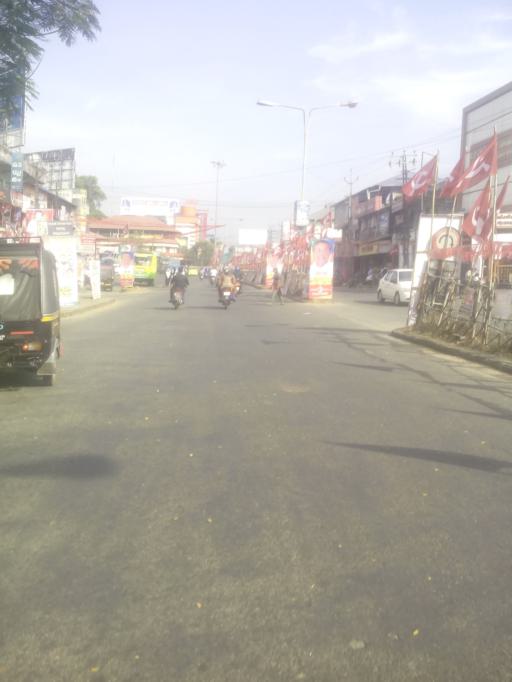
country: IN
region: Kerala
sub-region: Ernakulam
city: Perumpavur
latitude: 10.1152
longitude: 76.4737
